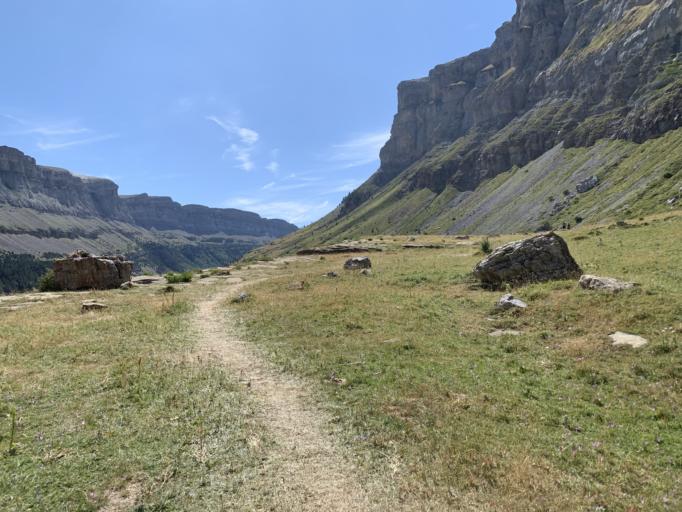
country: ES
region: Aragon
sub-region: Provincia de Huesca
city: Broto
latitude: 42.6490
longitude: 0.0145
